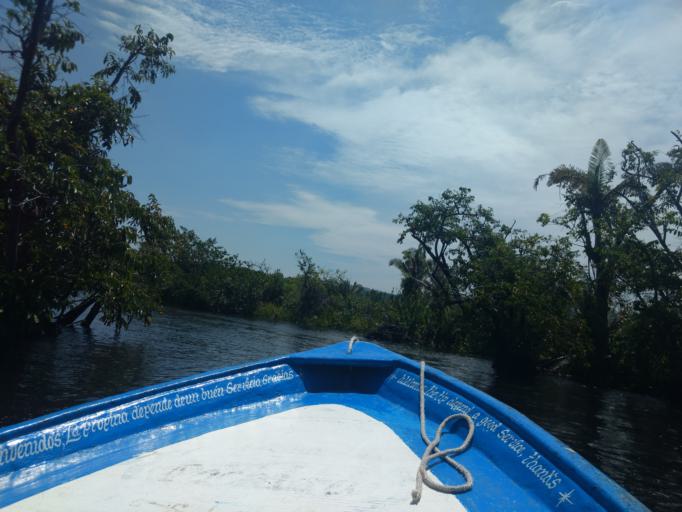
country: MX
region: Nayarit
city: San Blas
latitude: 21.5350
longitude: -105.2371
